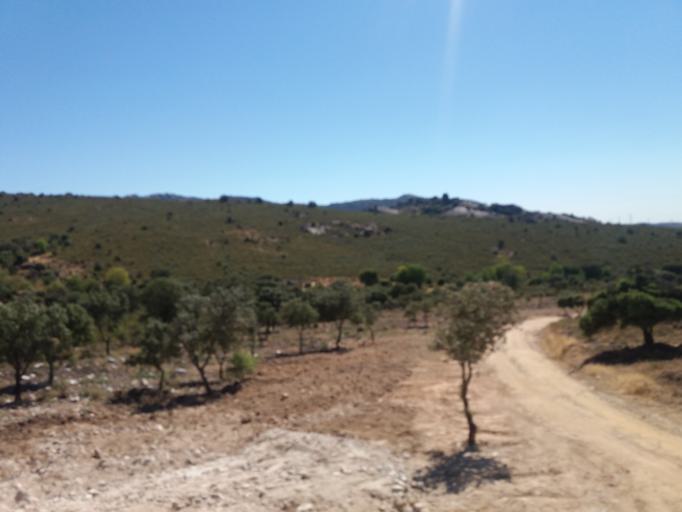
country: ES
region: Madrid
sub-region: Provincia de Madrid
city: Moralzarzal
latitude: 40.6378
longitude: -3.9586
